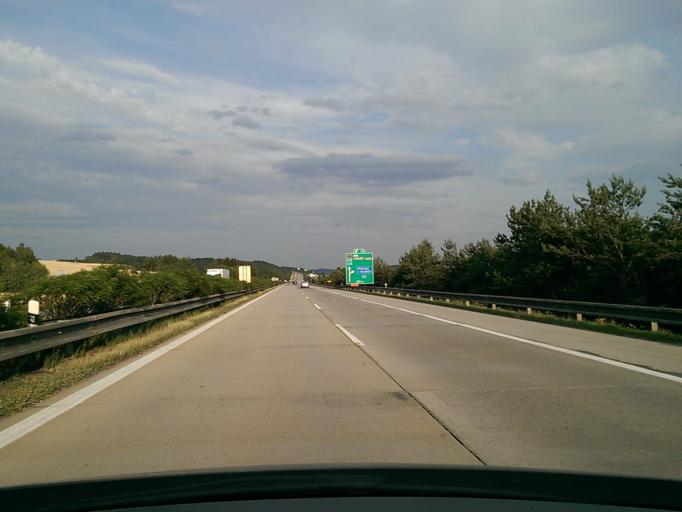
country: CZ
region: Vysocina
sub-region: Okres Zd'ar nad Sazavou
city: Velke Mezirici
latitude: 49.3748
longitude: 15.9579
